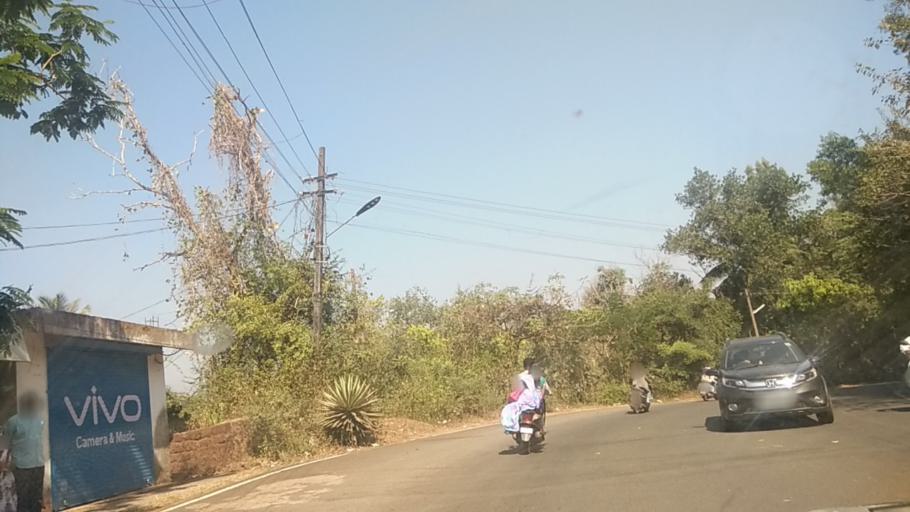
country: IN
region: Goa
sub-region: South Goa
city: Raia
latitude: 15.3388
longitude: 74.0158
